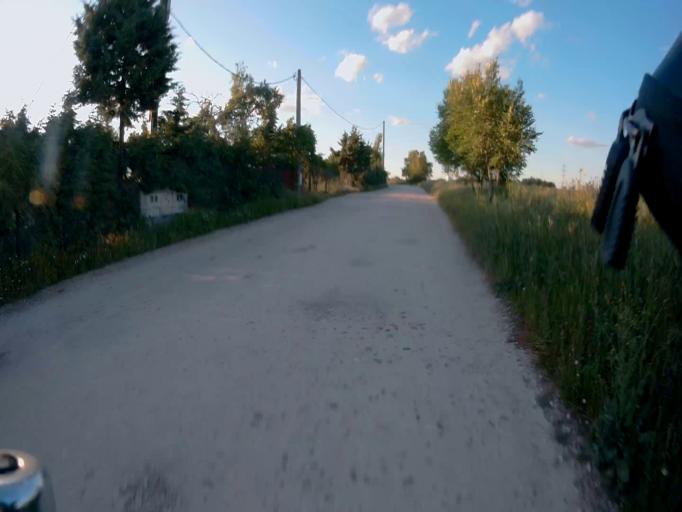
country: ES
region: Madrid
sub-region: Provincia de Madrid
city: Leganes
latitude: 40.3297
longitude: -3.7949
